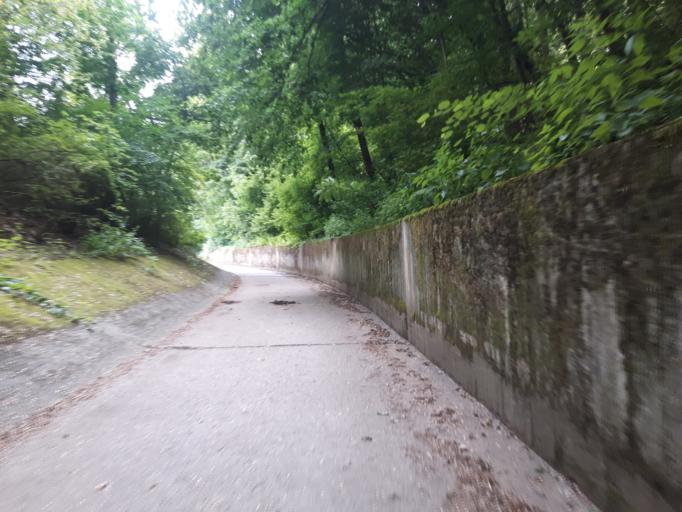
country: DE
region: Baden-Wuerttemberg
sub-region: Regierungsbezirk Stuttgart
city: Zaberfeld
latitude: 49.0524
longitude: 8.9373
